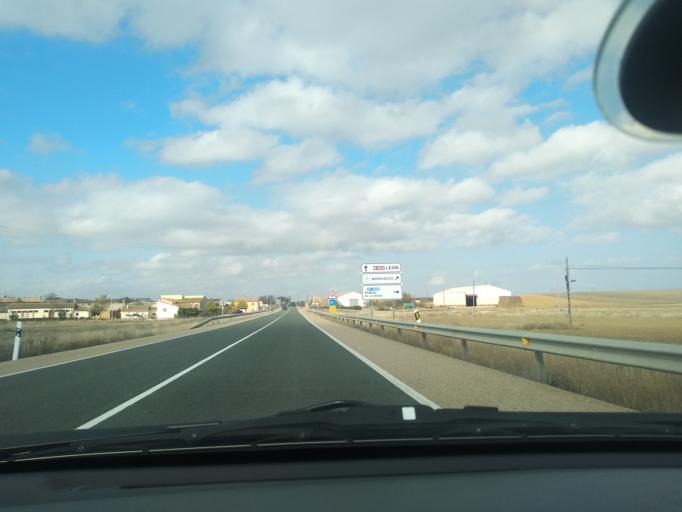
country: ES
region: Castille and Leon
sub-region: Provincia de Valladolid
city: Berrueces
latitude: 41.9448
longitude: -5.0928
